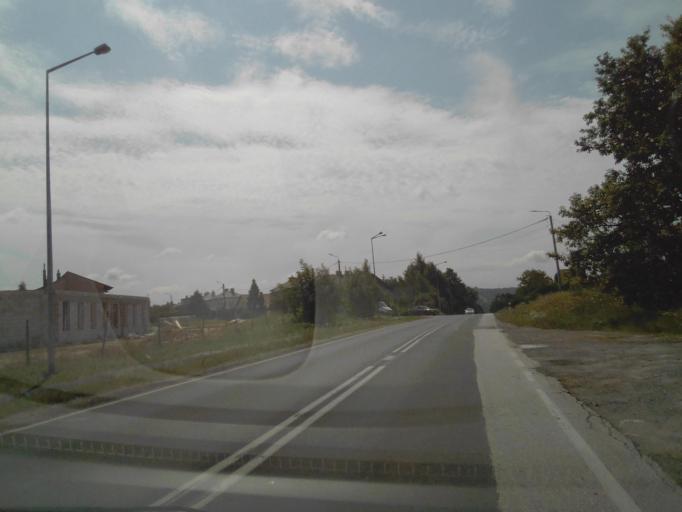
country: PL
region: Subcarpathian Voivodeship
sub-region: Powiat ropczycko-sedziszowski
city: Ropczyce
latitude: 50.0638
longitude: 21.5973
